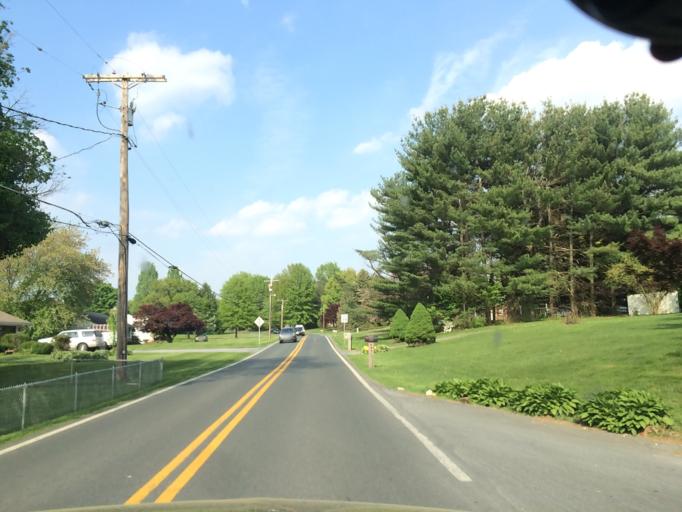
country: US
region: Maryland
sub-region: Carroll County
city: Eldersburg
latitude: 39.4710
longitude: -76.9611
